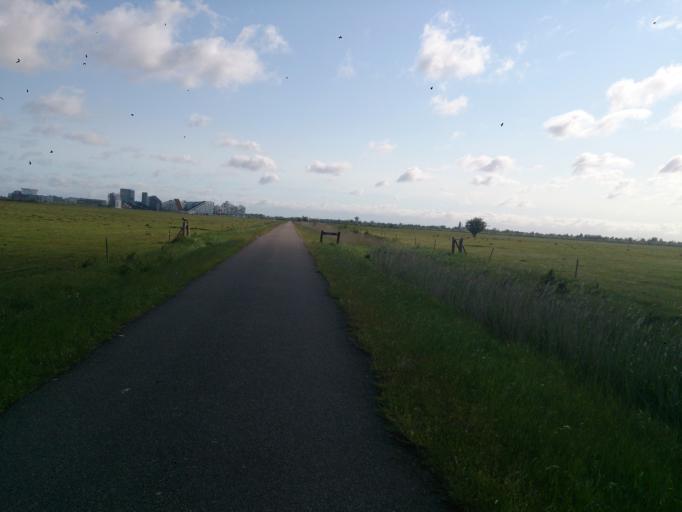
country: DK
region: Capital Region
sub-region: Tarnby Kommune
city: Tarnby
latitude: 55.6044
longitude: 12.5583
